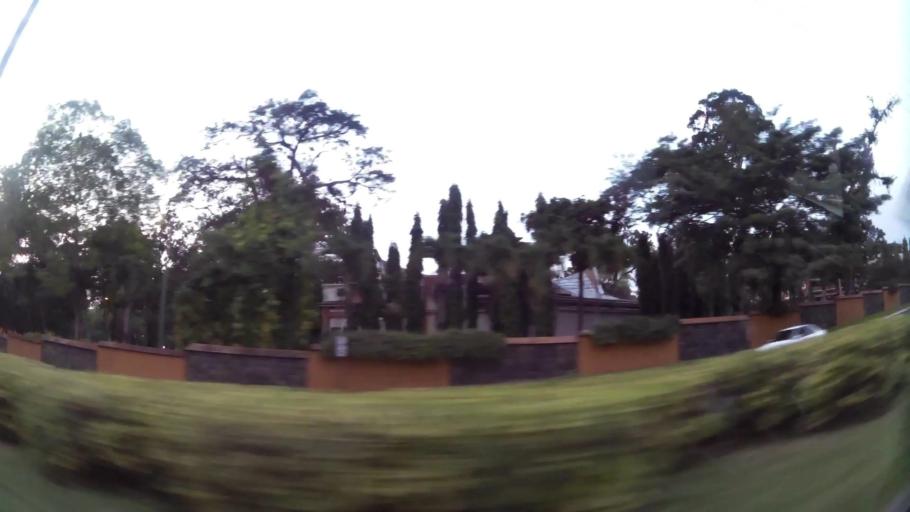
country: GT
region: Retalhuleu
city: San Martin Zapotitlan
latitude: 14.5973
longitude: -91.6139
